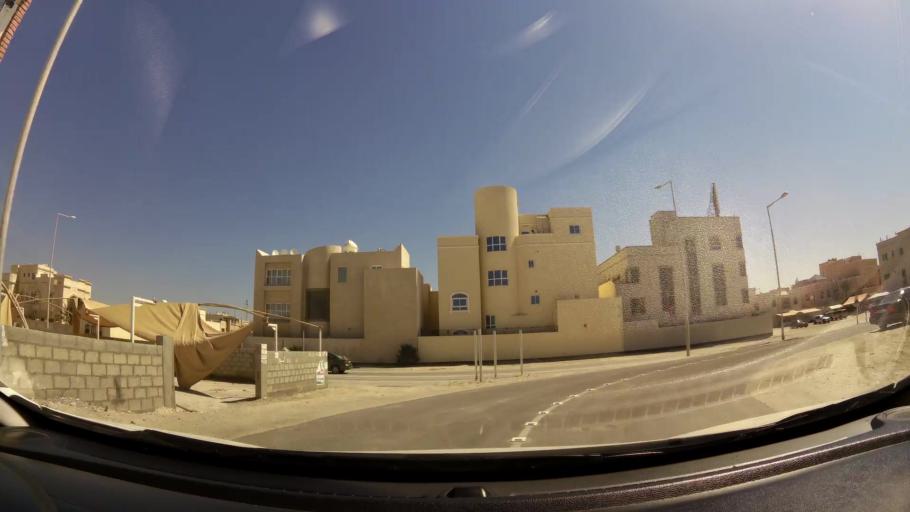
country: BH
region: Muharraq
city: Al Muharraq
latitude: 26.2740
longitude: 50.6026
